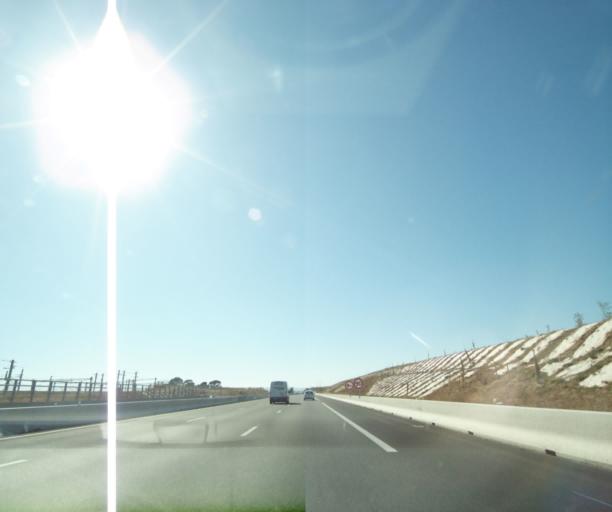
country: FR
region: Languedoc-Roussillon
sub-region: Departement de l'Herault
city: Lattes
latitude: 43.5956
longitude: 3.9223
